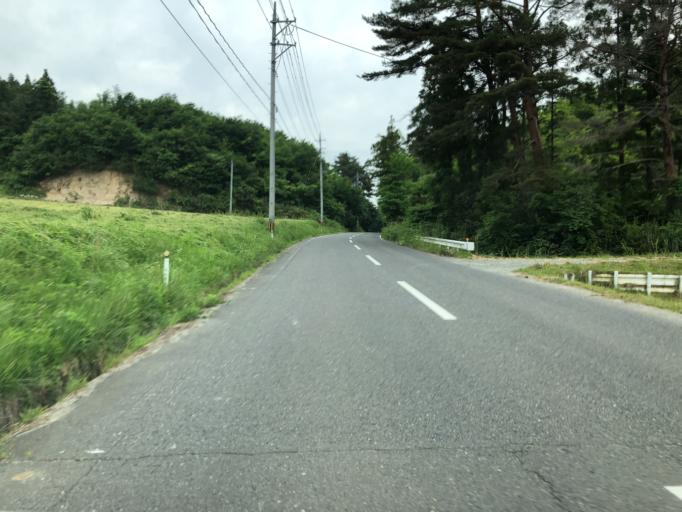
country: JP
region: Fukushima
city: Funehikimachi-funehiki
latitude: 37.4279
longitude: 140.6212
